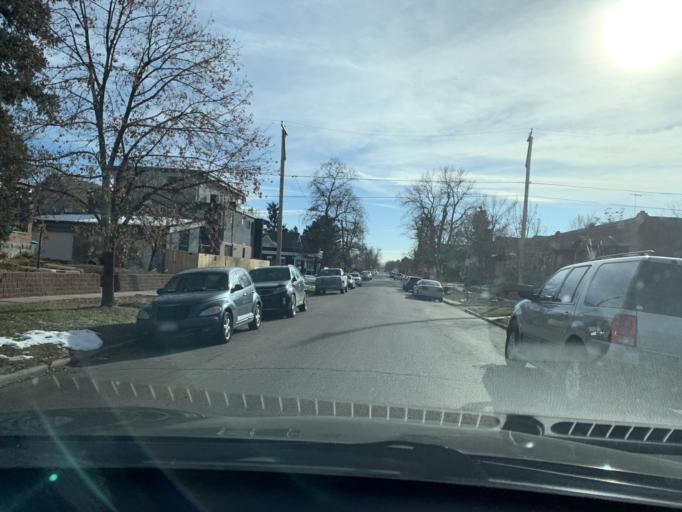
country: US
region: Colorado
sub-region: Jefferson County
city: Edgewater
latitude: 39.7520
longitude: -105.0316
